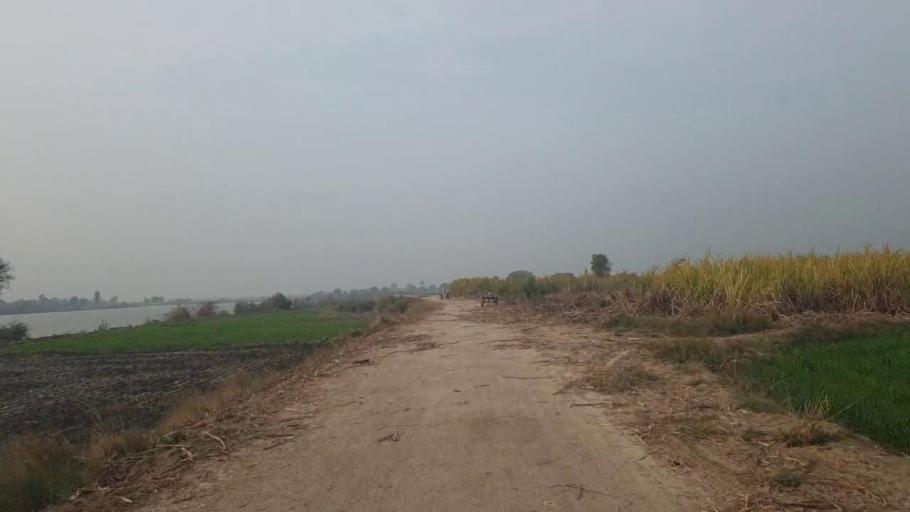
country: PK
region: Sindh
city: Berani
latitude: 25.8209
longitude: 68.7352
